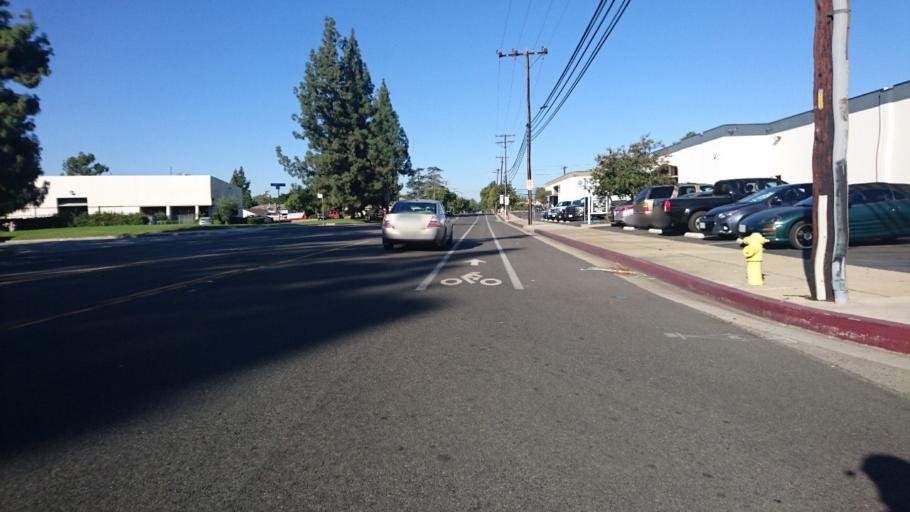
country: US
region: California
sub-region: Los Angeles County
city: La Verne
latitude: 34.0976
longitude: -117.7544
